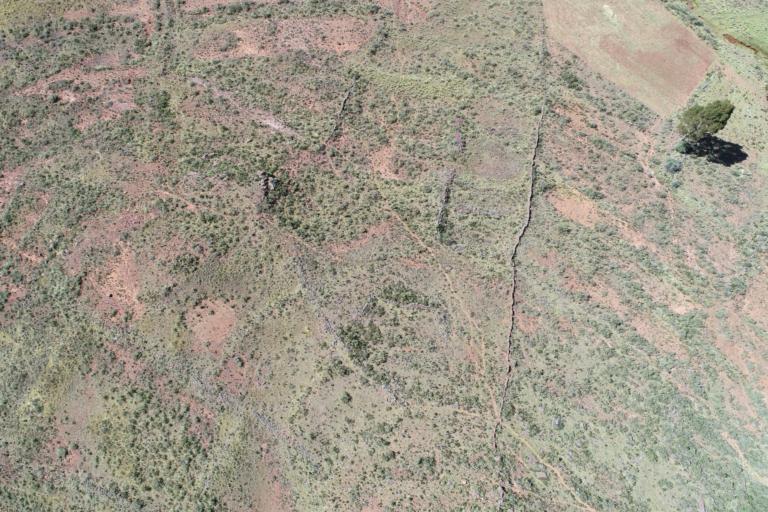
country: BO
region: La Paz
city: Tiahuanaco
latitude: -16.6060
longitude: -68.7743
